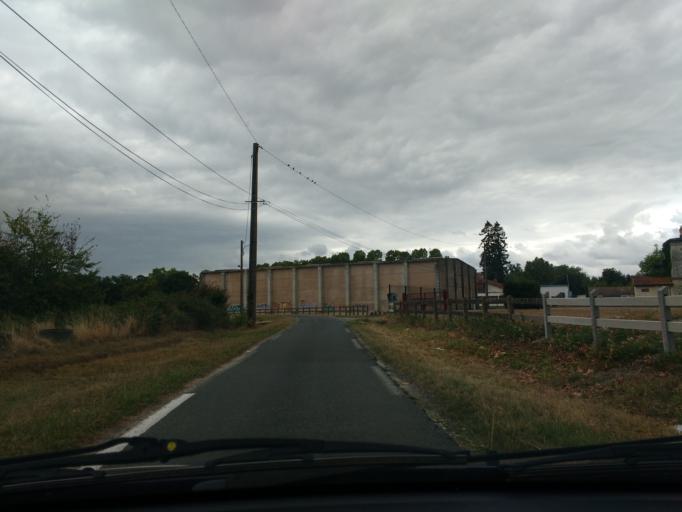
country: FR
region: Aquitaine
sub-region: Departement de la Gironde
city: Canejan
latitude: 44.7792
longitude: -0.6281
